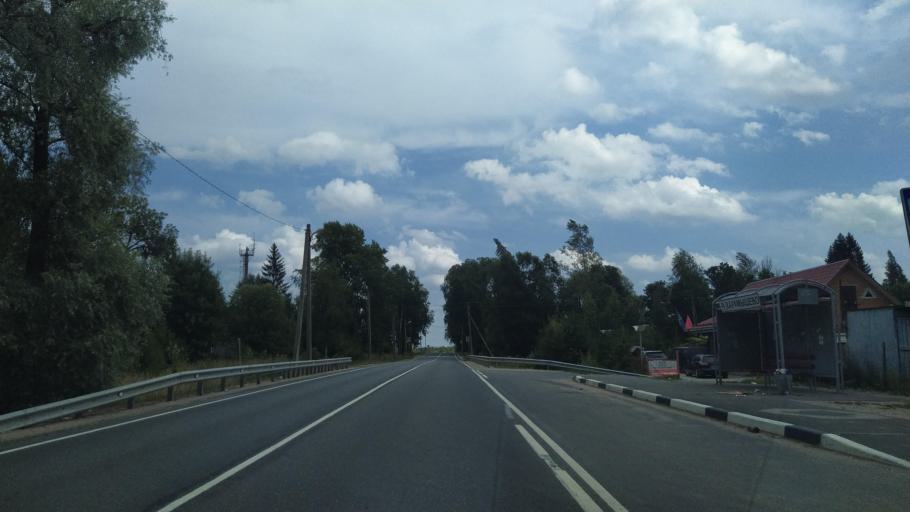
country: RU
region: Pskov
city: Pskov
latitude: 57.7612
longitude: 28.7621
